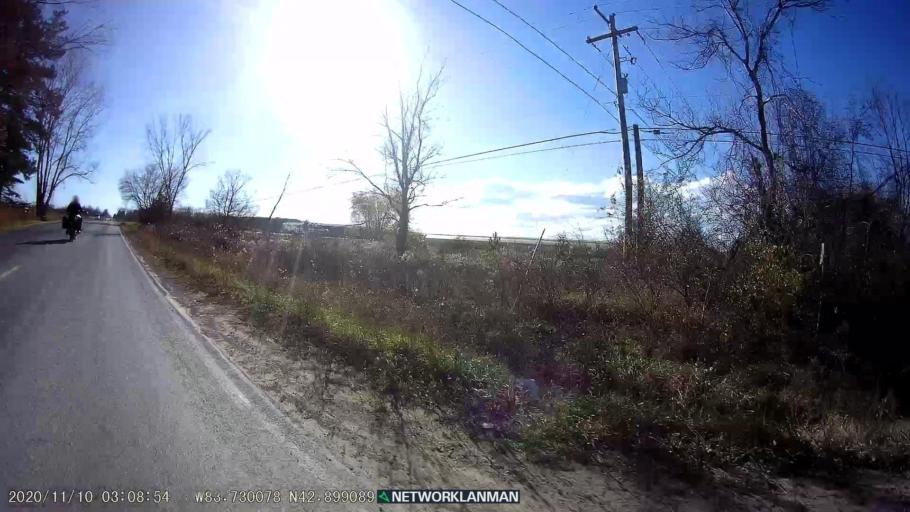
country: US
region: Michigan
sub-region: Genesee County
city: Lake Fenton
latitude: 42.8989
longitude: -83.7300
